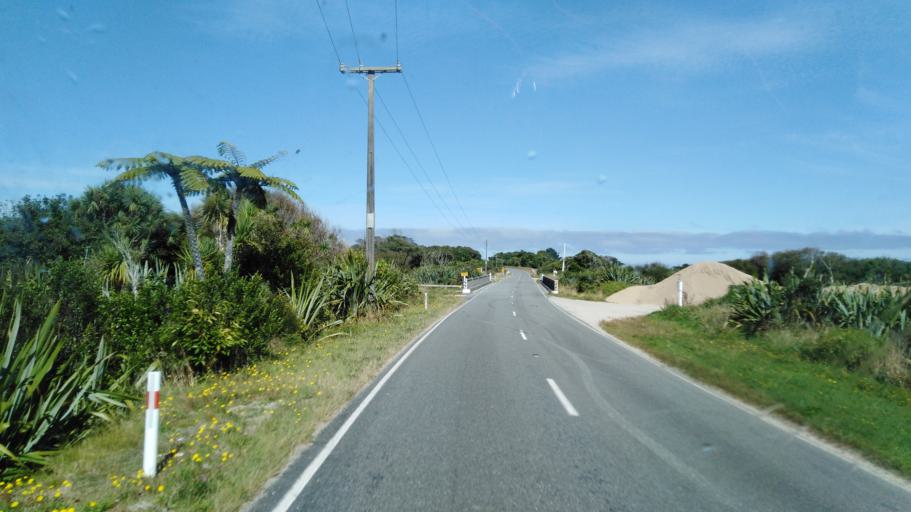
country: NZ
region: West Coast
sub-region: Buller District
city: Westport
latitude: -41.2897
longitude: 172.1007
